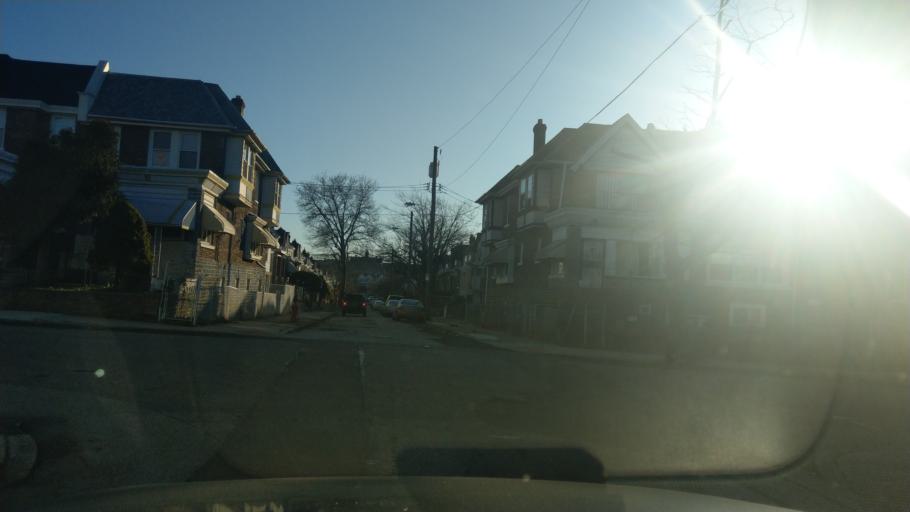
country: US
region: Pennsylvania
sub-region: Montgomery County
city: Wyncote
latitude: 40.0560
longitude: -75.1467
